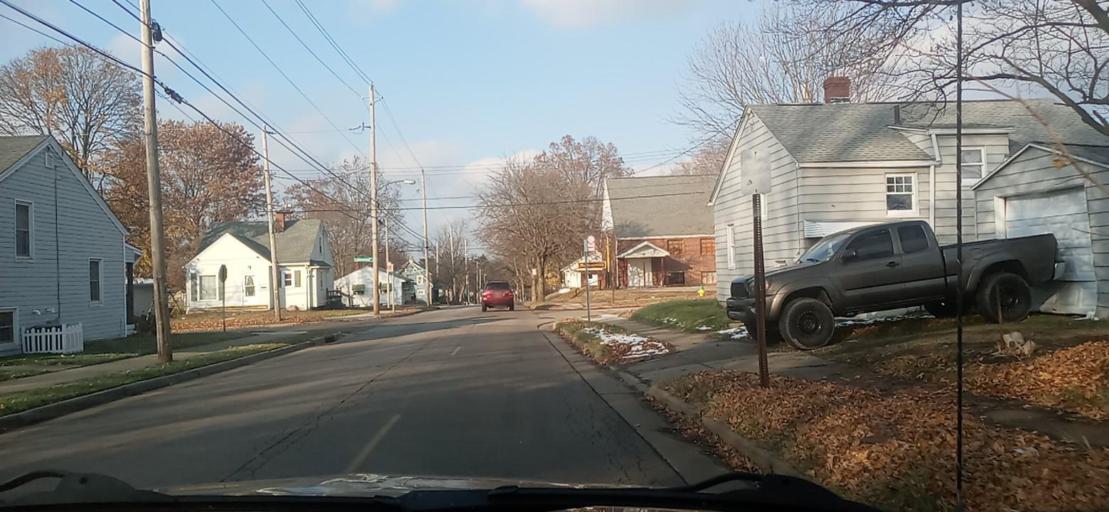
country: US
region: Ohio
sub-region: Summit County
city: Akron
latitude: 41.0556
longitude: -81.5572
